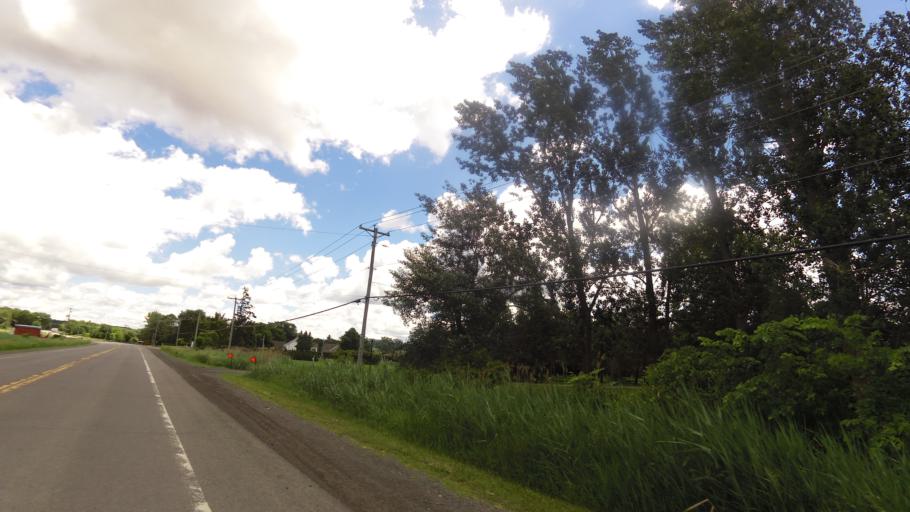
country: CA
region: Quebec
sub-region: Monteregie
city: Hudson
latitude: 45.5290
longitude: -74.1917
